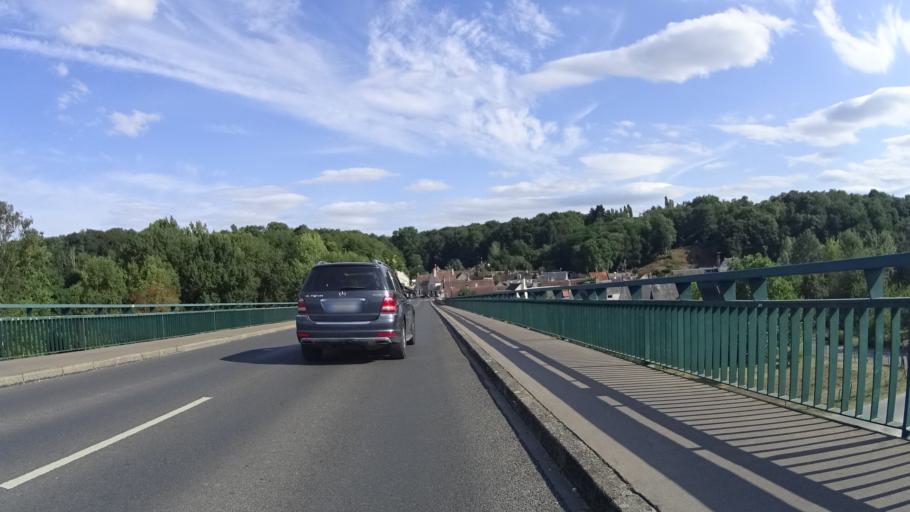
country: FR
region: Centre
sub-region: Departement du Loir-et-Cher
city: Chaumont-sur-Loire
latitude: 47.4839
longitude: 1.1918
